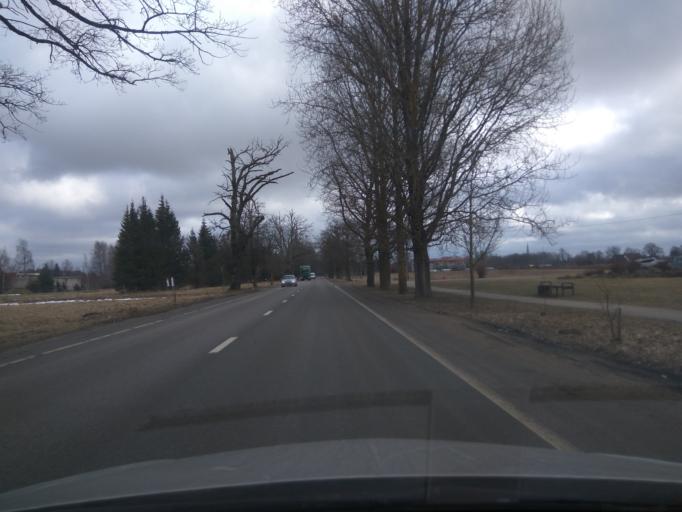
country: LV
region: Kuldigas Rajons
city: Kuldiga
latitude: 57.2759
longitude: 22.0263
